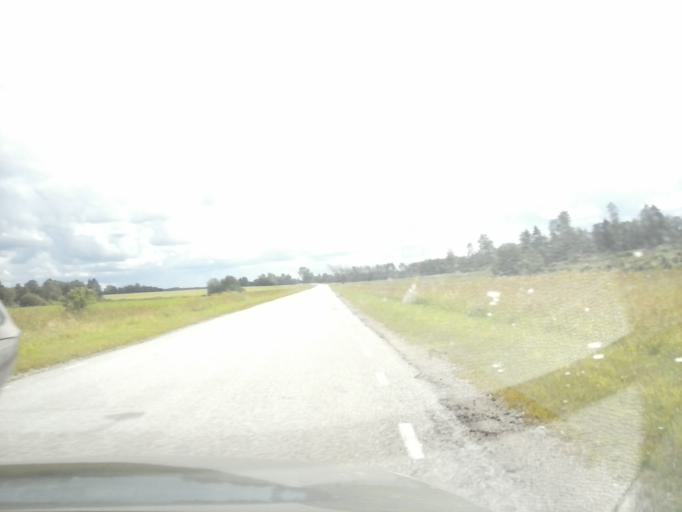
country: EE
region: Jaervamaa
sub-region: Koeru vald
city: Koeru
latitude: 59.0300
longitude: 26.0885
